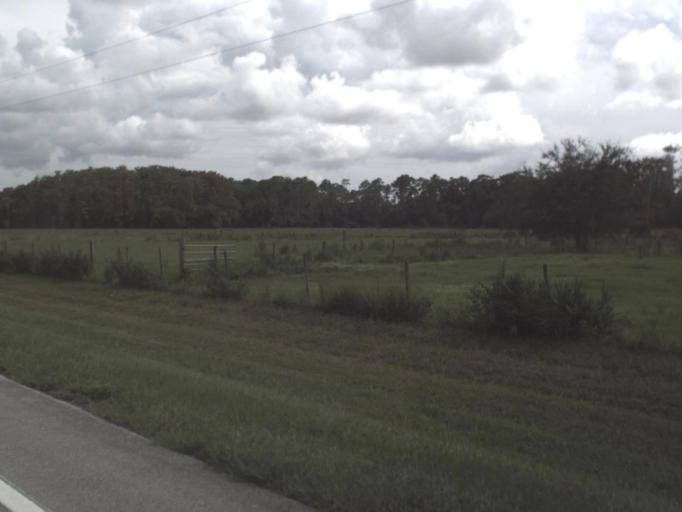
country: US
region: Florida
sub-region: DeSoto County
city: Nocatee
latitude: 27.2034
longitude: -81.9984
